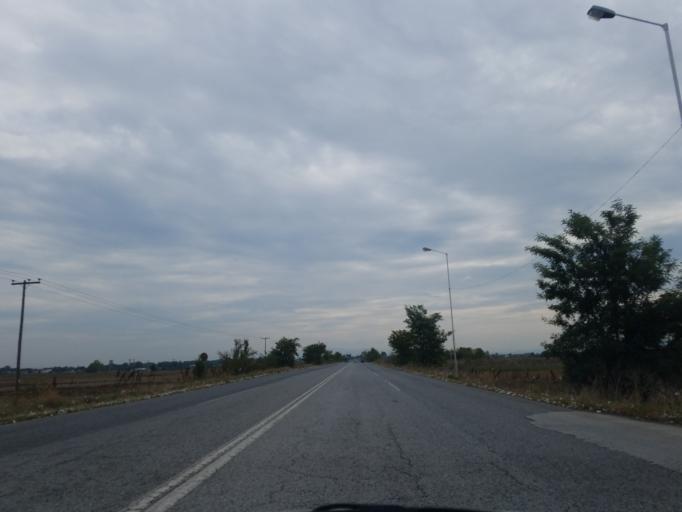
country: GR
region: Thessaly
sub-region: Nomos Kardhitsas
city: Sofades
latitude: 39.3484
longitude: 22.0699
